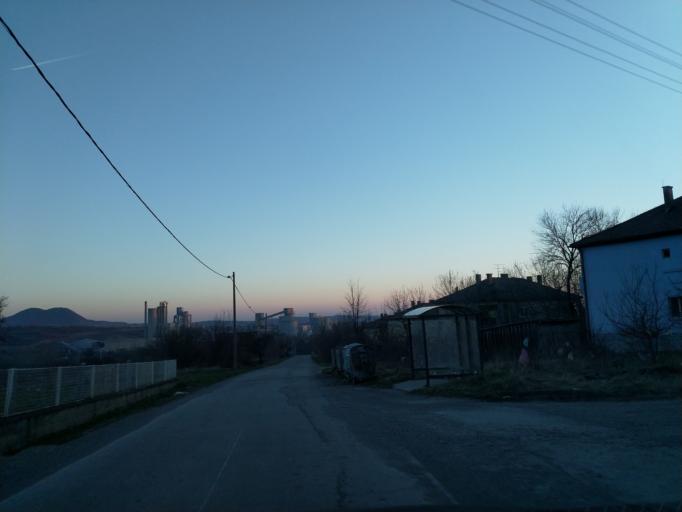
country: RS
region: Central Serbia
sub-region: Pomoravski Okrug
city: Paracin
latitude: 43.9194
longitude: 21.5106
